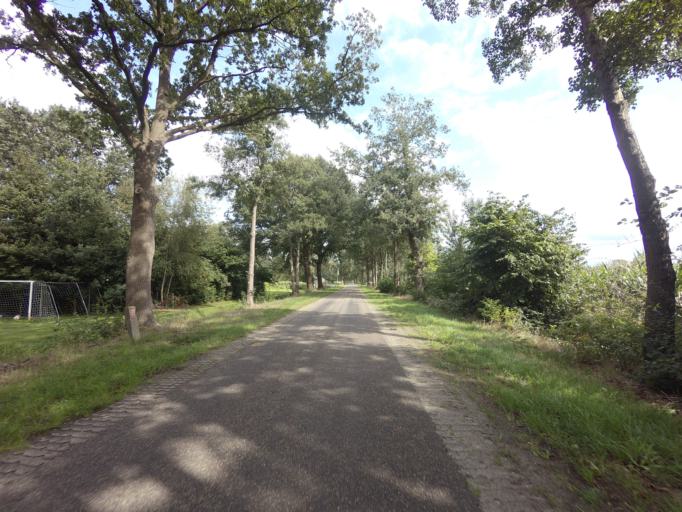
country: NL
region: Drenthe
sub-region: Gemeente De Wolden
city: Ruinen
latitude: 52.7424
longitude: 6.3561
